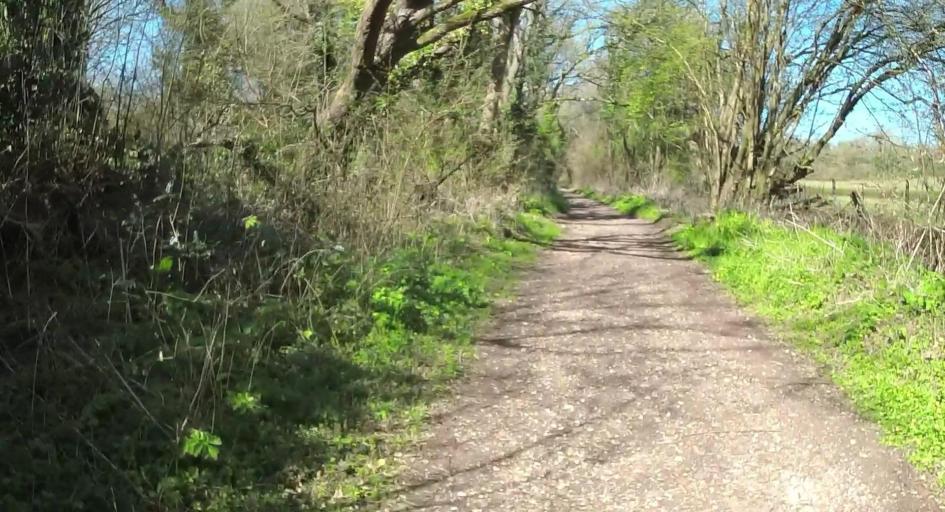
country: GB
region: England
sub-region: Hampshire
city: Abbotts Ann
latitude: 51.0957
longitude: -1.4971
